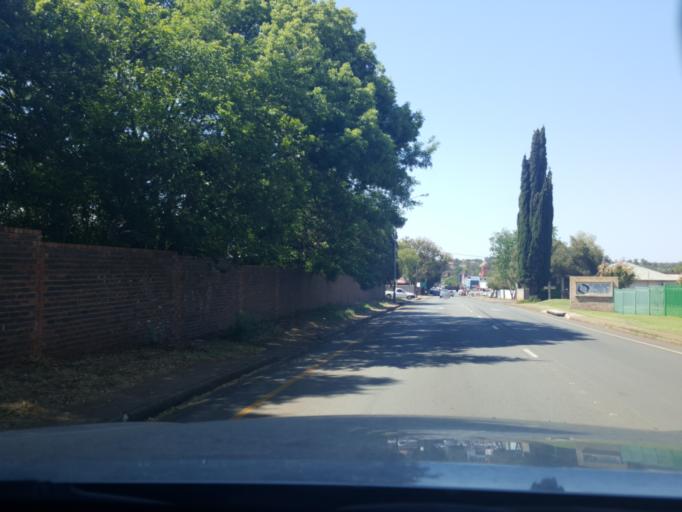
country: ZA
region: North-West
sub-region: Ngaka Modiri Molema District Municipality
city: Zeerust
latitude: -25.5421
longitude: 26.0793
